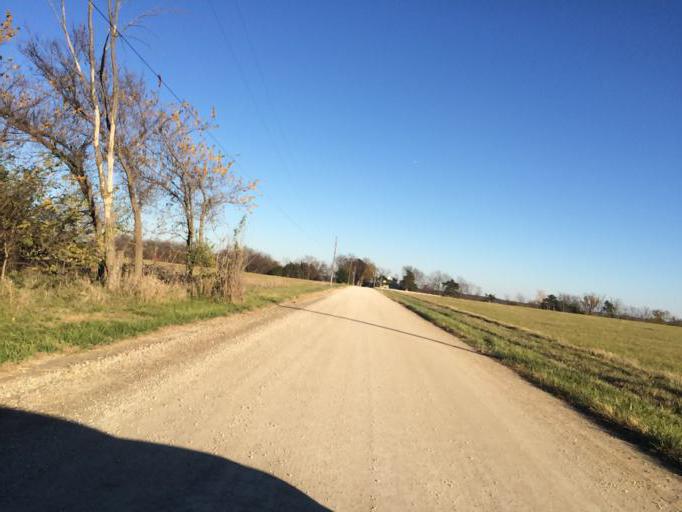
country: US
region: Kansas
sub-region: Douglas County
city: Lawrence
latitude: 38.8947
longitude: -95.3386
